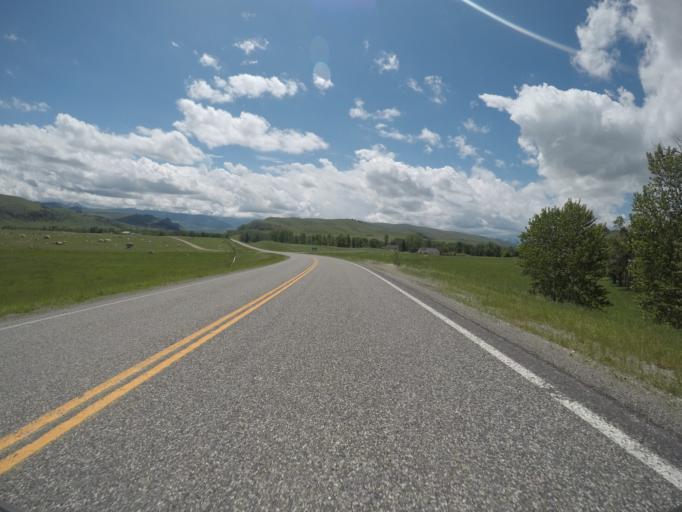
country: US
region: Montana
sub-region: Sweet Grass County
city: Big Timber
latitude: 45.6657
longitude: -110.1121
